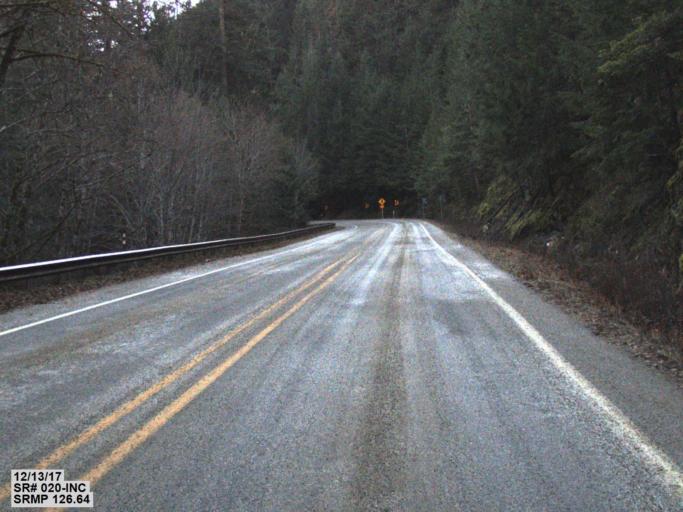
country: US
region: Washington
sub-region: Snohomish County
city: Darrington
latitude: 48.7116
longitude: -121.1478
